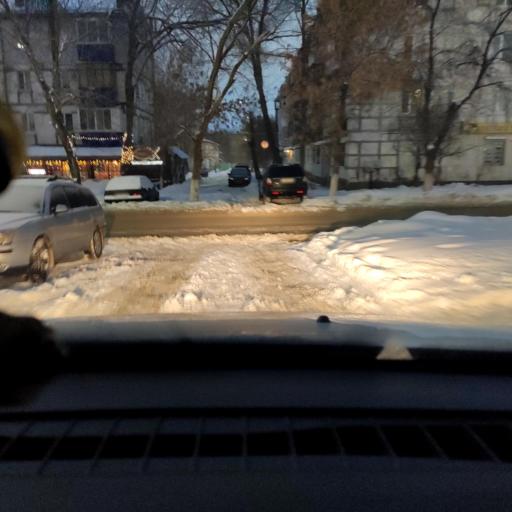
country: RU
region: Samara
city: Novokuybyshevsk
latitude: 53.0960
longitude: 49.9564
